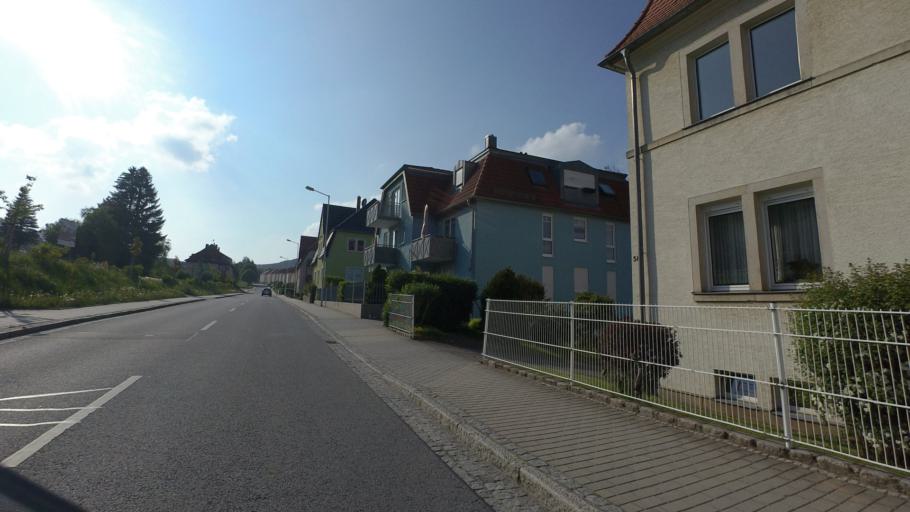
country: DE
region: Saxony
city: Sebnitz
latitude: 50.9823
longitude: 14.2734
